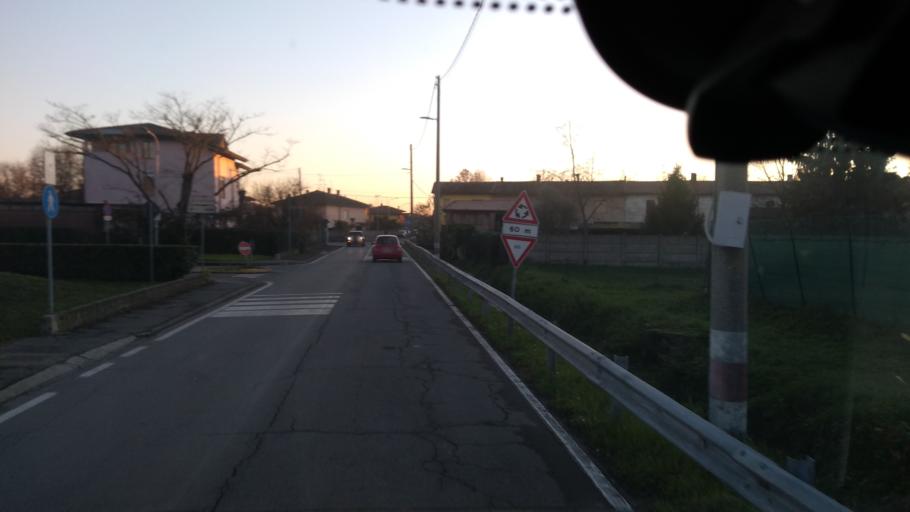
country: IT
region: Lombardy
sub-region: Provincia di Bergamo
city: Arzago d'Adda
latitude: 45.4816
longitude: 9.5647
